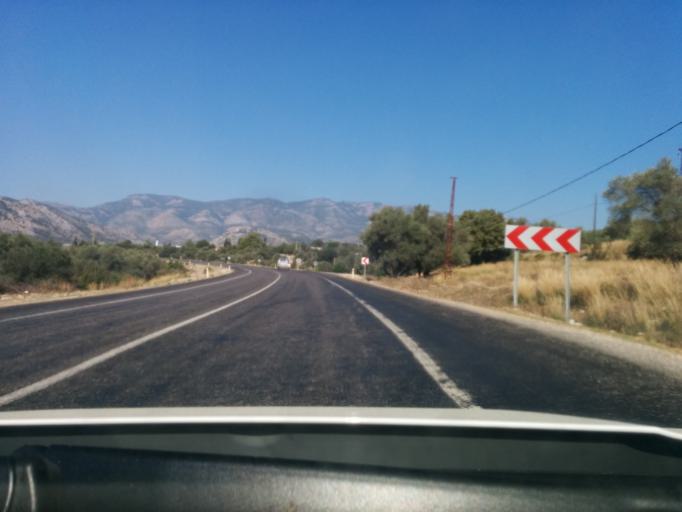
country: TR
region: Mugla
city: Esen
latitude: 36.4079
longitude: 29.2830
